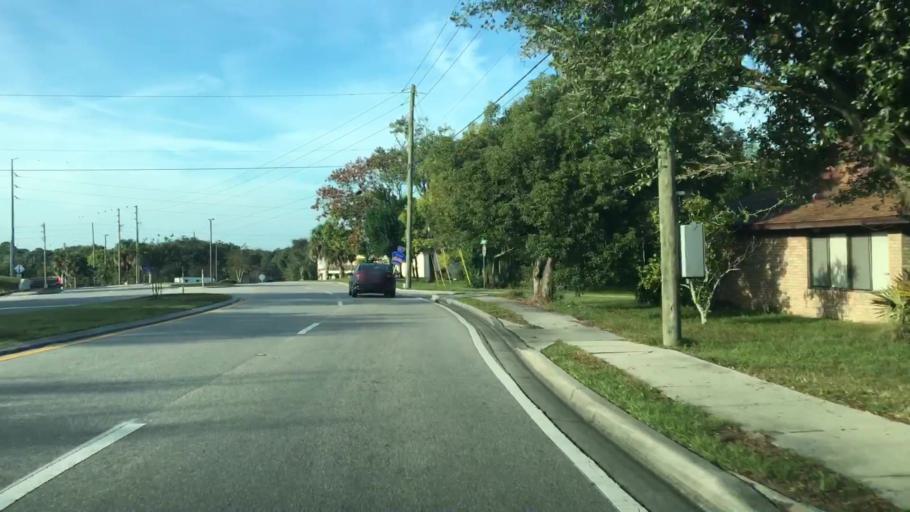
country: US
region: Florida
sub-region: Volusia County
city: Deltona
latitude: 28.9116
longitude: -81.2586
